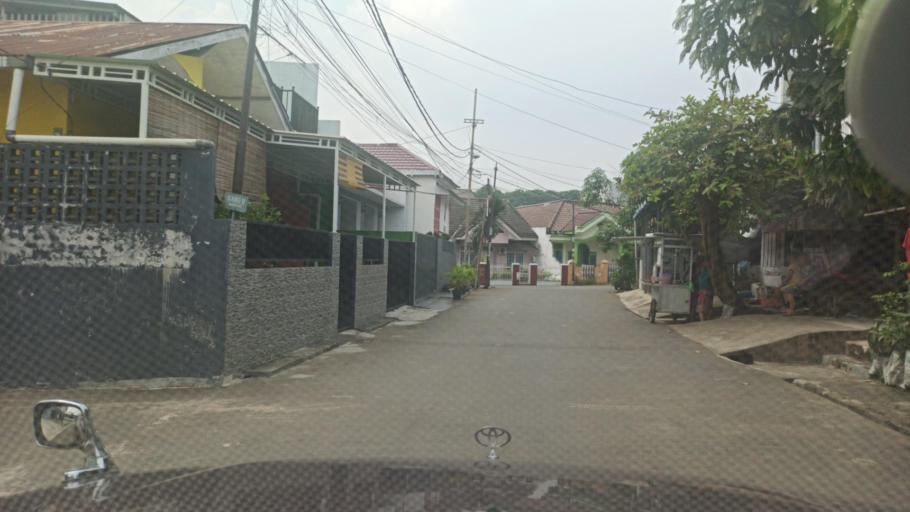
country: ID
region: South Sumatra
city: Plaju
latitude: -2.9906
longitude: 104.7391
